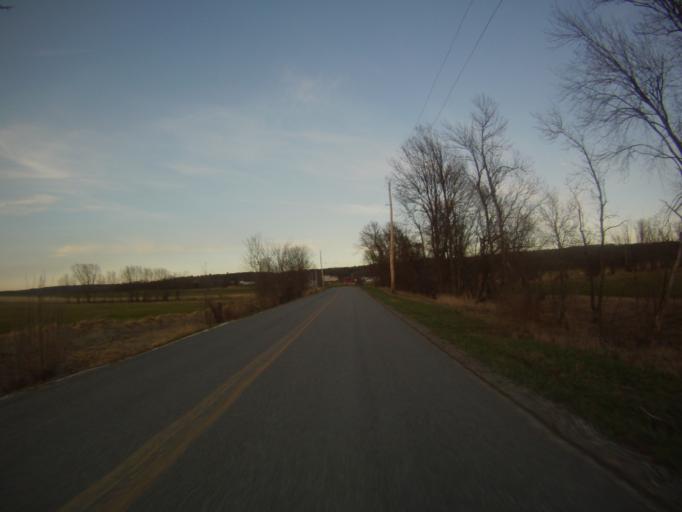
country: US
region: Vermont
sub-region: Addison County
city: Middlebury (village)
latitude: 44.0196
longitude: -73.2380
